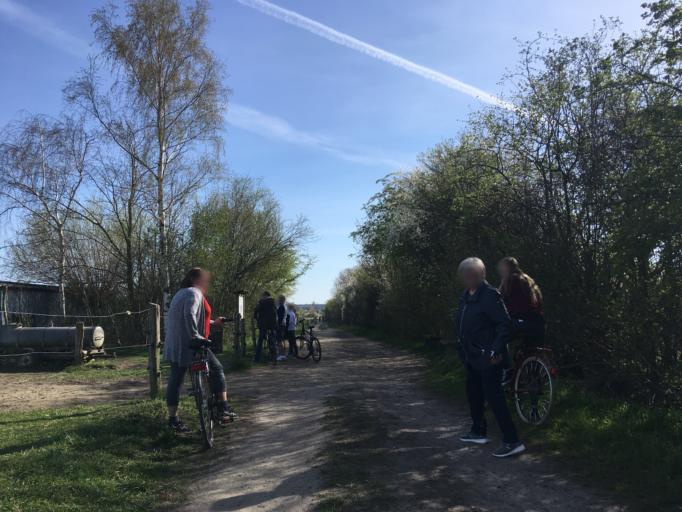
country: DE
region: Berlin
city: Wartenberg
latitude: 52.5898
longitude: 13.5105
